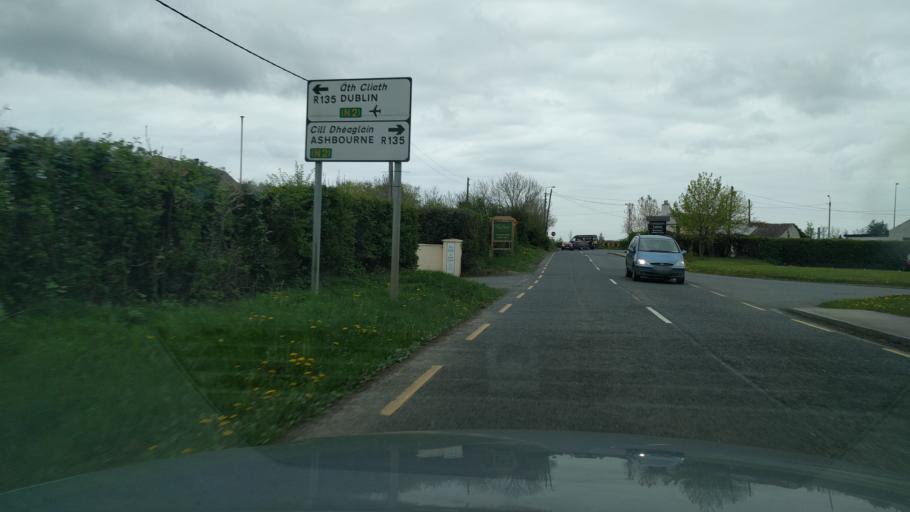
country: IE
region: Leinster
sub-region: An Mhi
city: Ashbourne
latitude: 53.4590
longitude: -6.3488
